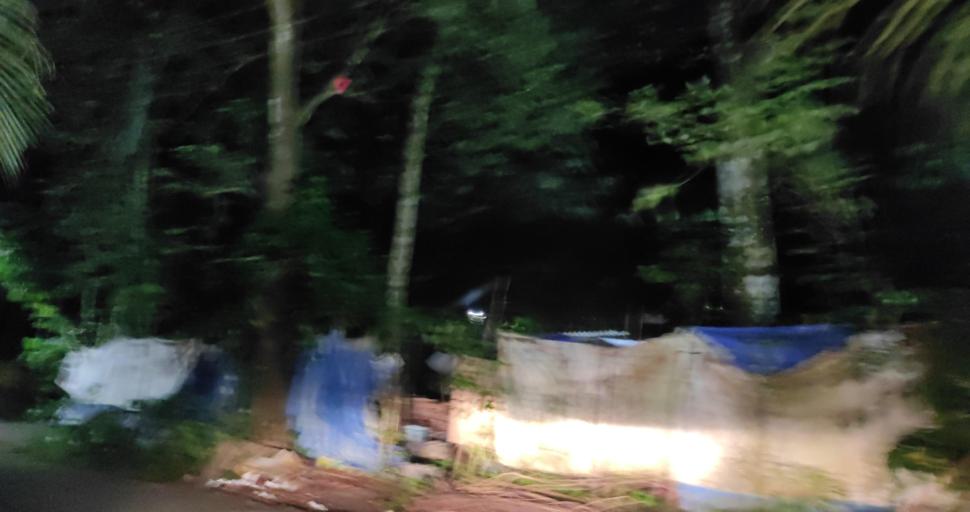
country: IN
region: Kerala
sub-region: Alappuzha
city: Vayalar
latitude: 9.6851
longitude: 76.3137
